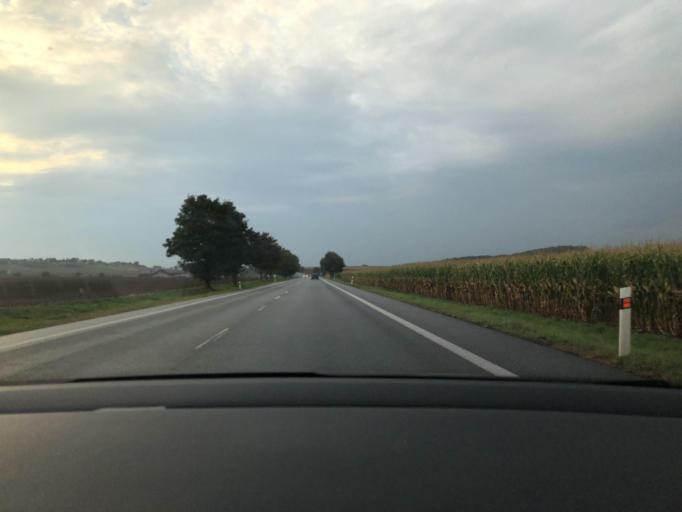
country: CZ
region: Central Bohemia
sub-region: Okres Kolin
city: Kolin
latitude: 50.0344
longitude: 15.1560
